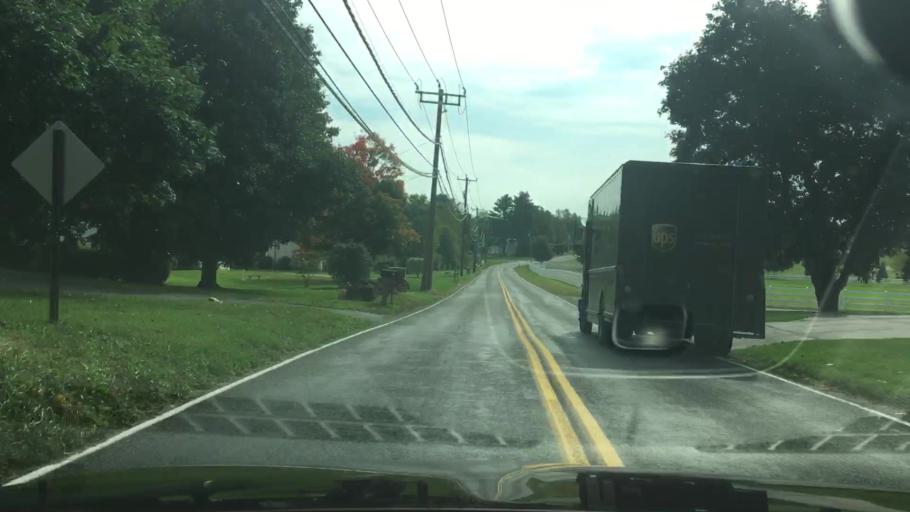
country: US
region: Connecticut
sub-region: Tolland County
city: Somers
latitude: 41.9798
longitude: -72.4872
